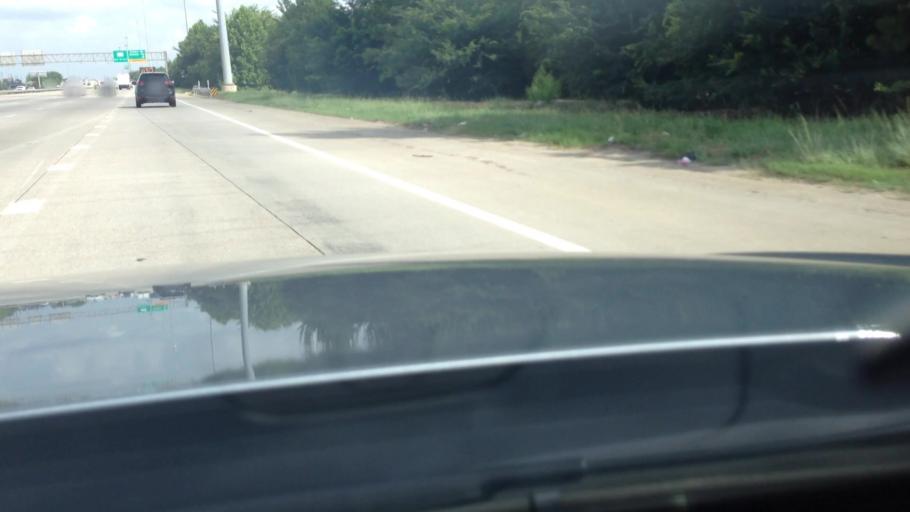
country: US
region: Texas
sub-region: Harris County
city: Hudson
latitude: 29.9483
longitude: -95.5307
